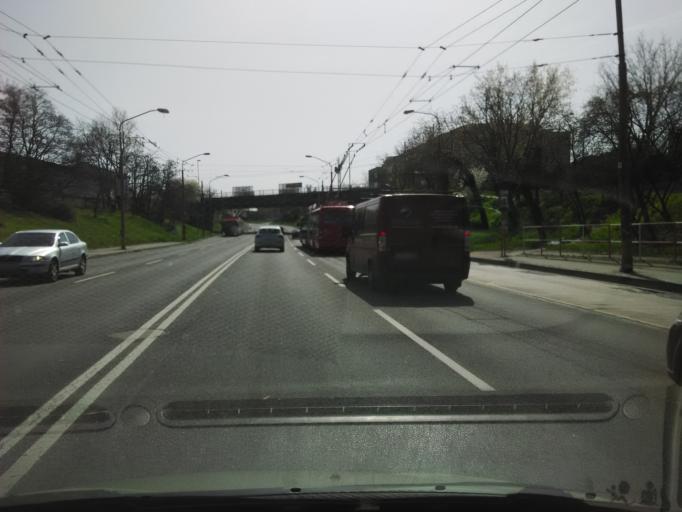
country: SK
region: Bratislavsky
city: Bratislava
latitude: 48.1465
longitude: 17.1856
